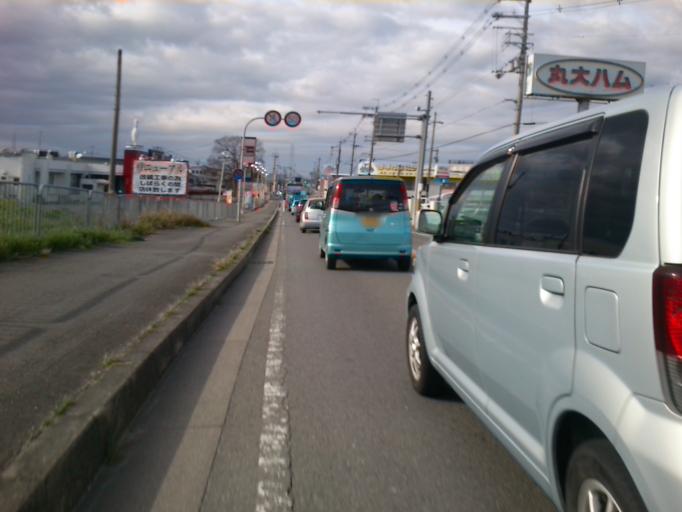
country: JP
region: Kyoto
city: Tanabe
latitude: 34.8248
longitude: 135.7942
